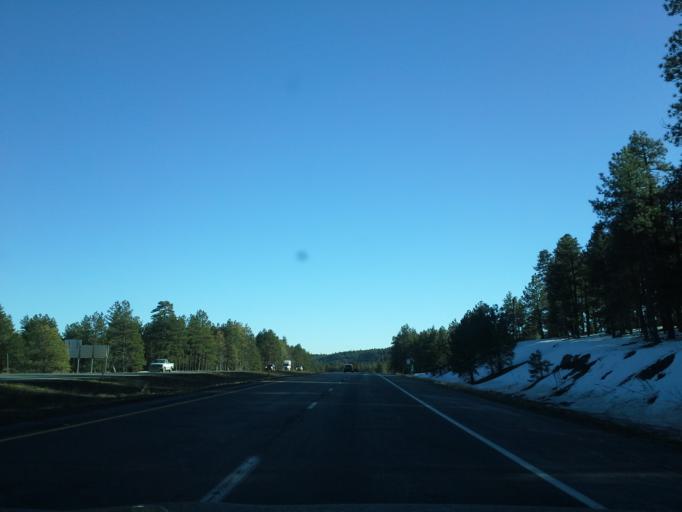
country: US
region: Arizona
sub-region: Coconino County
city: Mountainaire
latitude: 34.9658
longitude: -111.6819
